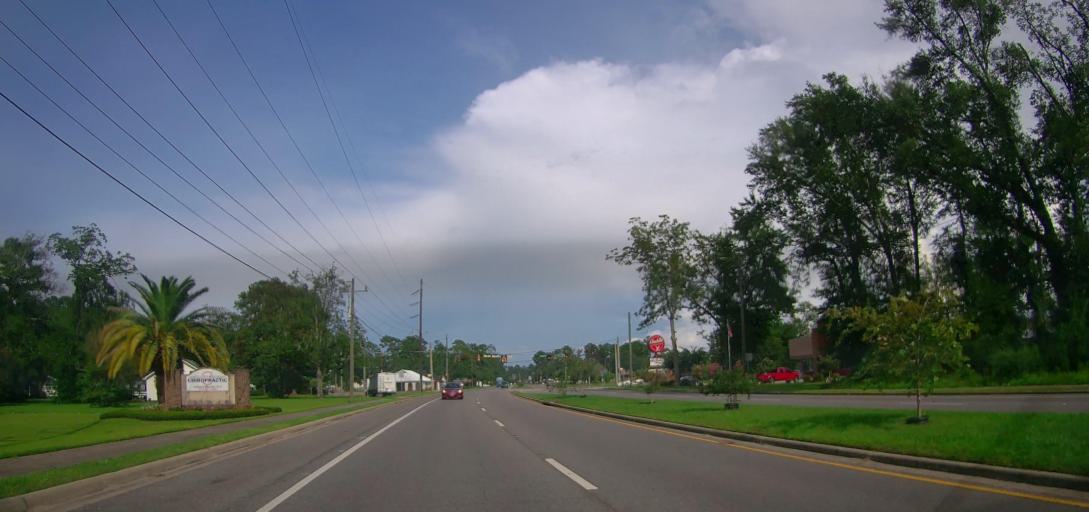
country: US
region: Georgia
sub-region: Wayne County
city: Jesup
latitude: 31.6041
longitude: -81.9019
